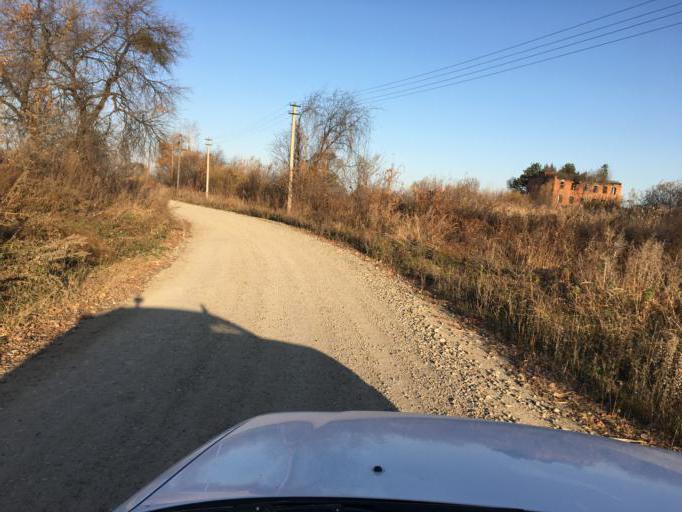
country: RU
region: Primorskiy
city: Lazo
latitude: 45.8630
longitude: 133.6452
